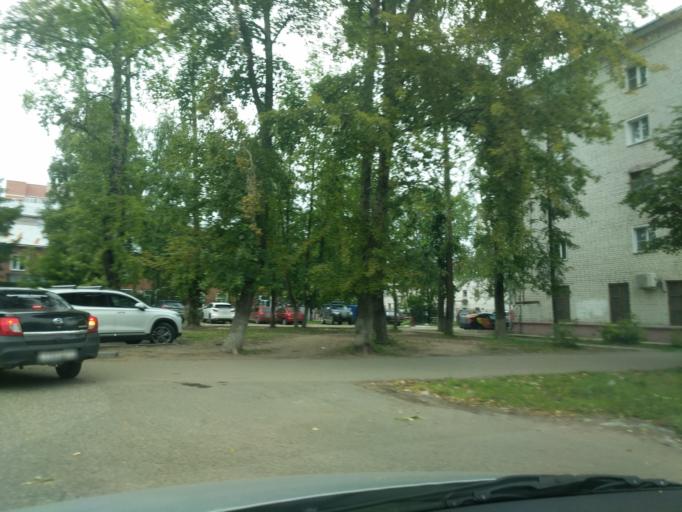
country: RU
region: Kirov
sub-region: Kirovo-Chepetskiy Rayon
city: Kirov
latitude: 58.6376
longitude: 49.6193
